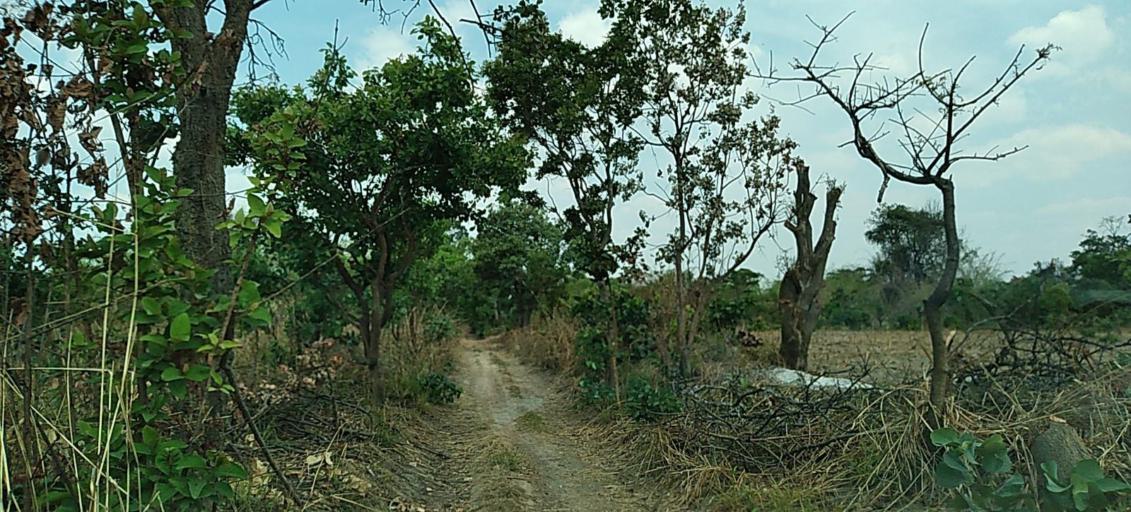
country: ZM
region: Copperbelt
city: Chililabombwe
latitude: -12.3405
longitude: 27.7813
